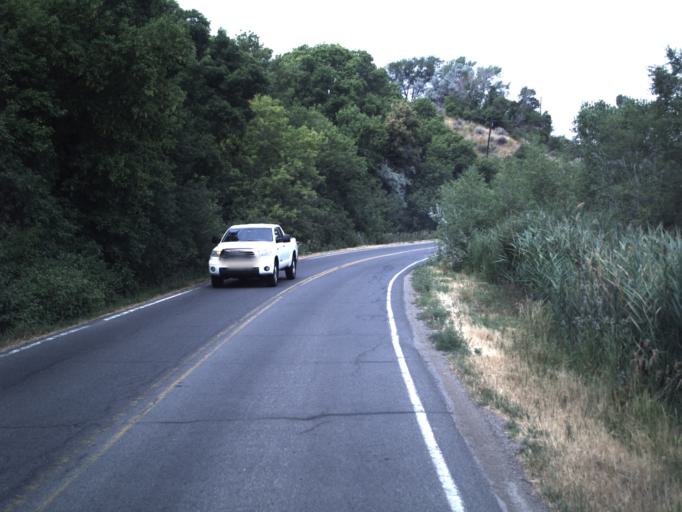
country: US
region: Utah
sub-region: Weber County
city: Washington Terrace
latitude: 41.1512
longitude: -111.9898
